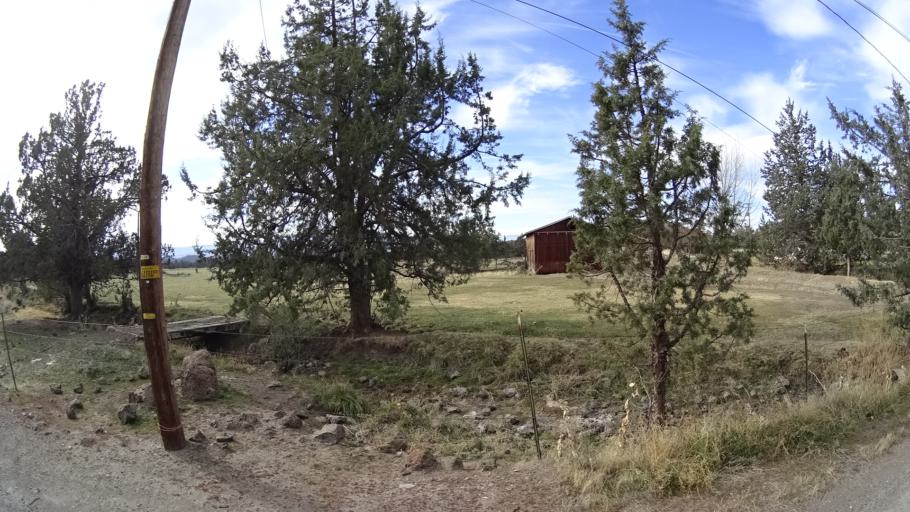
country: US
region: California
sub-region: Siskiyou County
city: Montague
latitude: 41.6488
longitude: -122.4189
